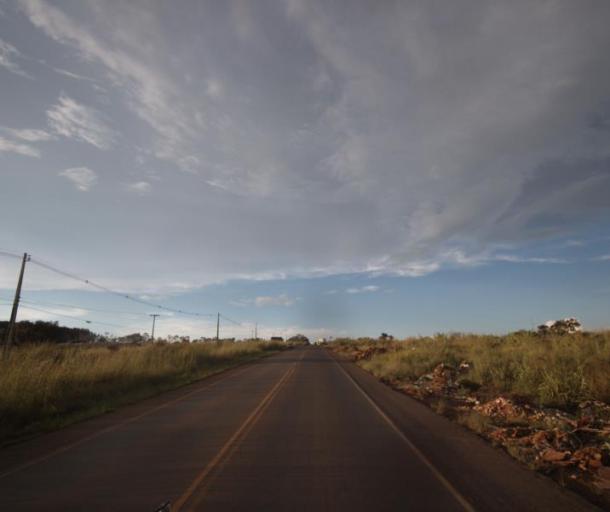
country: BR
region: Goias
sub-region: Anapolis
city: Anapolis
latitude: -16.2662
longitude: -48.9389
